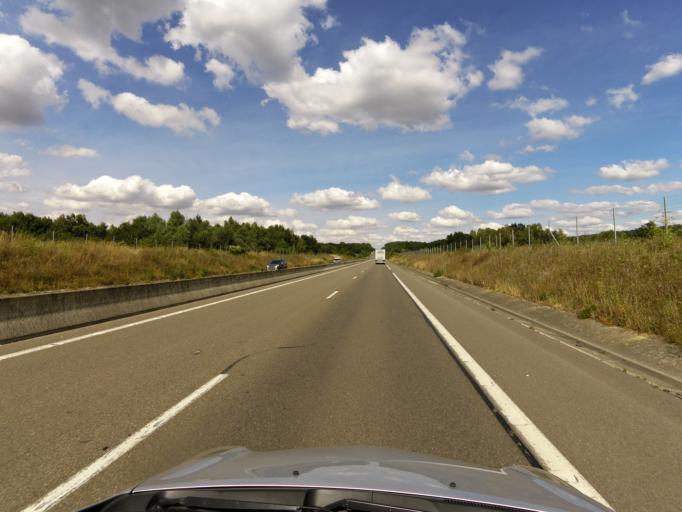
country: FR
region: Picardie
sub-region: Departement de l'Aisne
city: Vailly-sur-Aisne
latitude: 49.4813
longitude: 3.5386
